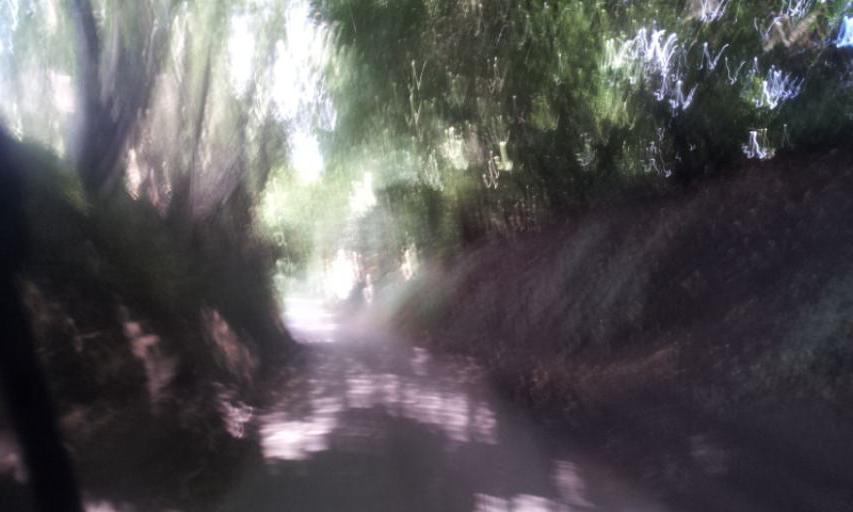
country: GB
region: England
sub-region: Kent
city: Snodland
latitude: 51.3234
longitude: 0.4169
